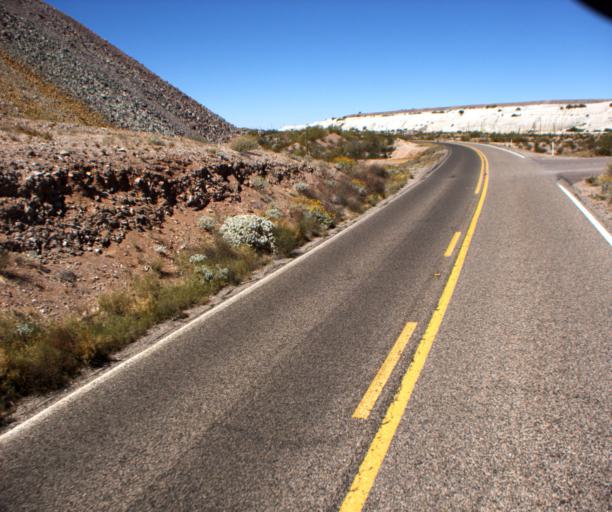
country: US
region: Arizona
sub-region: Pima County
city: Ajo
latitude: 32.3659
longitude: -112.8388
